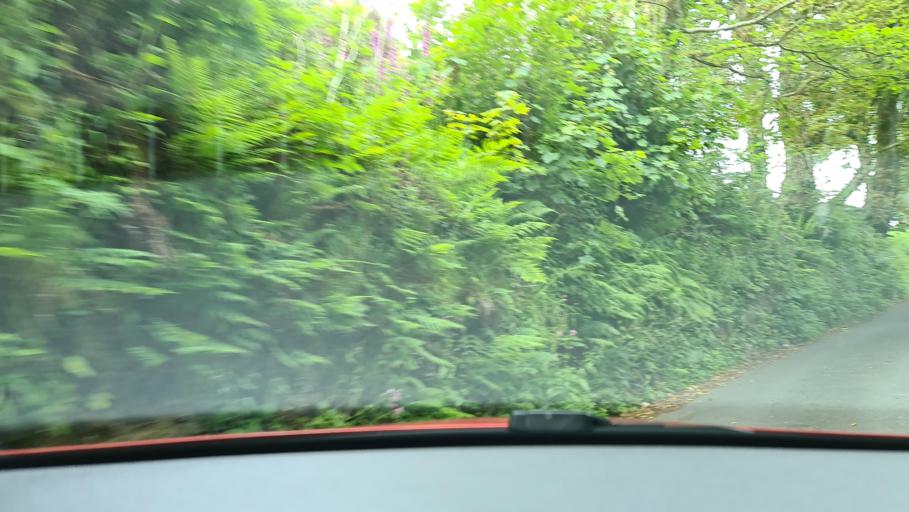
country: GB
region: England
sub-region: Cornwall
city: Camelford
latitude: 50.6200
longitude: -4.6995
